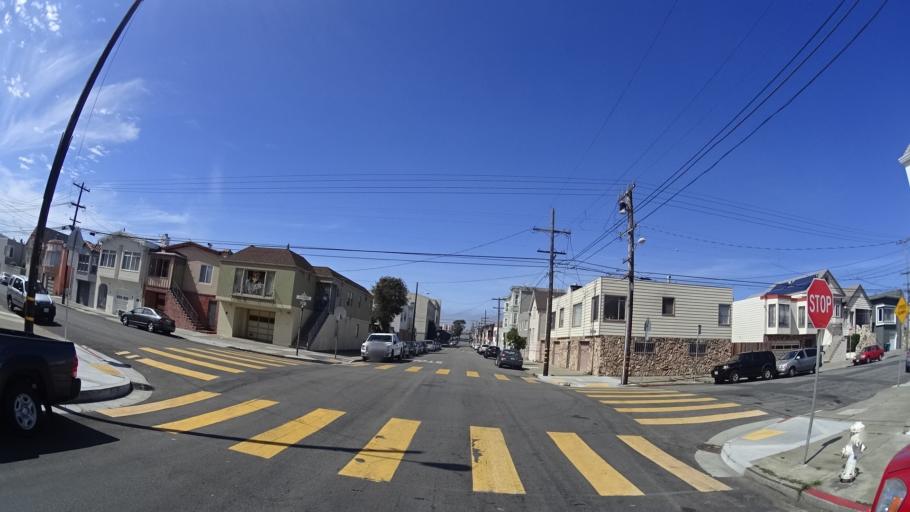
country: US
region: California
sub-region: San Mateo County
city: Daly City
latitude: 37.7153
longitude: -122.4329
